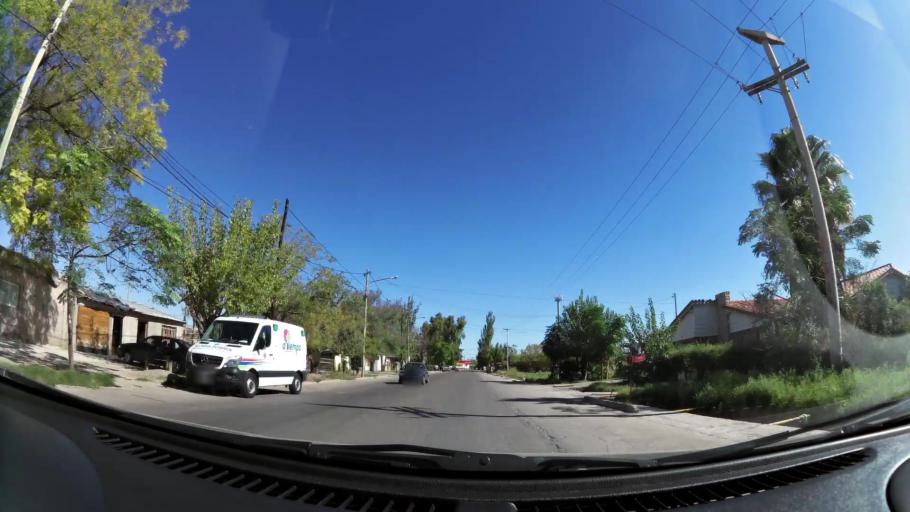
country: AR
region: Mendoza
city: Las Heras
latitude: -32.8403
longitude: -68.8113
